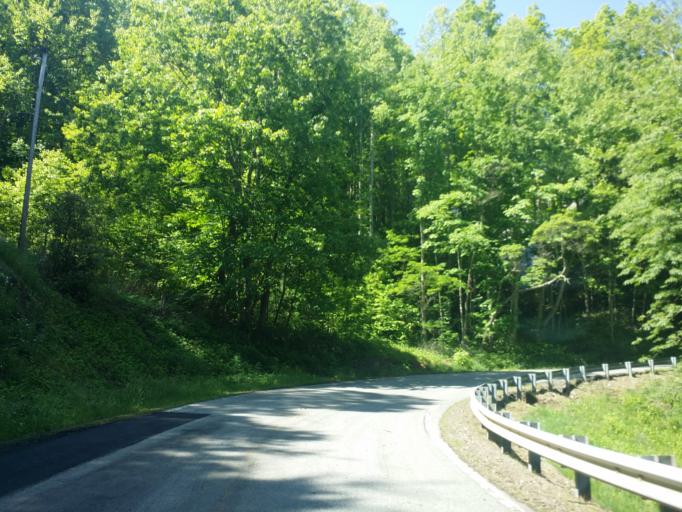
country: US
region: North Carolina
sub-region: Madison County
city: Marshall
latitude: 35.7207
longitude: -82.8379
